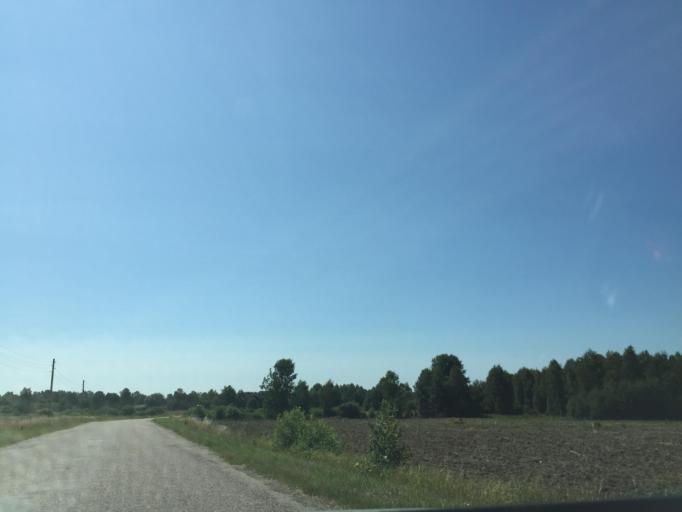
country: LV
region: Talsu Rajons
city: Stende
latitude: 57.1381
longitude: 22.6555
